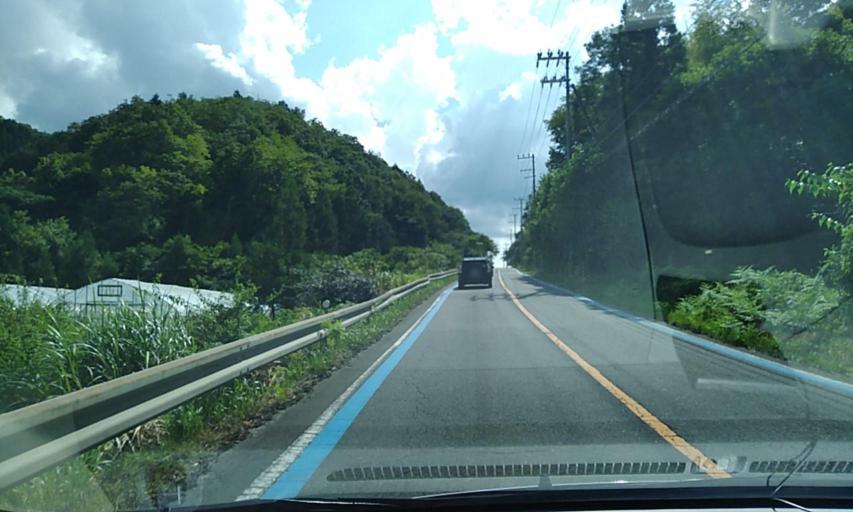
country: JP
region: Kyoto
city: Ayabe
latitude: 35.3159
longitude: 135.3107
